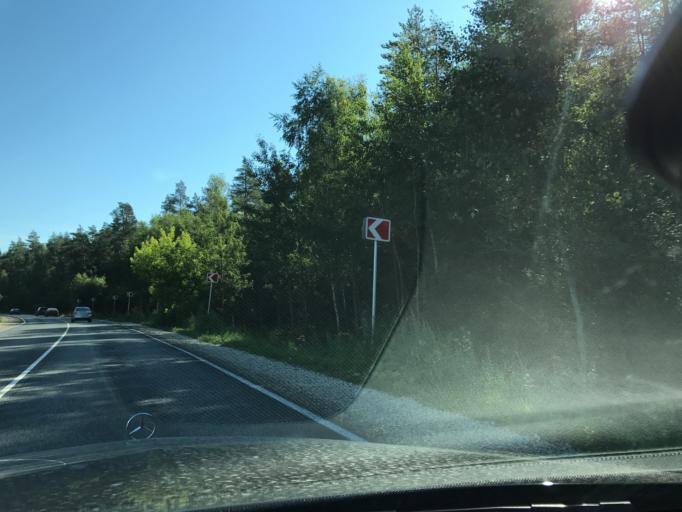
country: RU
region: Vladimir
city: Kirzhach
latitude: 56.1136
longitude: 38.7446
